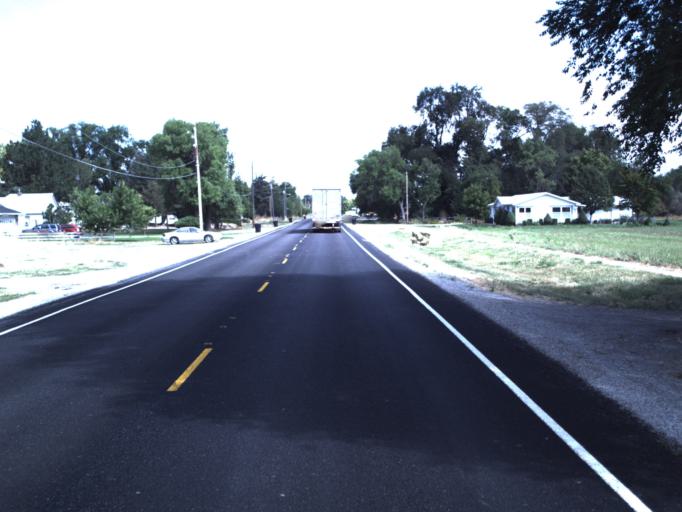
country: US
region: Utah
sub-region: Box Elder County
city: Honeyville
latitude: 41.6039
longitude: -112.1273
